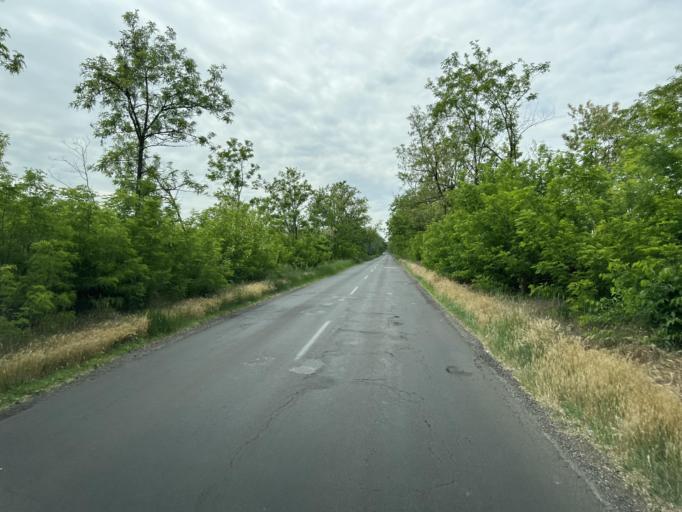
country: HU
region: Pest
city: Tapioszecso
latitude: 47.4678
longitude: 19.6163
